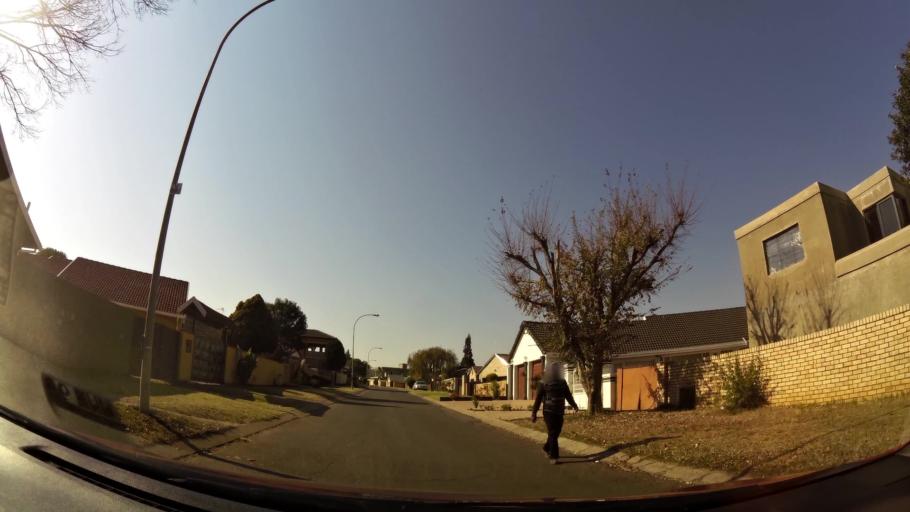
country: ZA
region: Gauteng
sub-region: City of Johannesburg Metropolitan Municipality
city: Soweto
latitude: -26.2490
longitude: 27.9550
